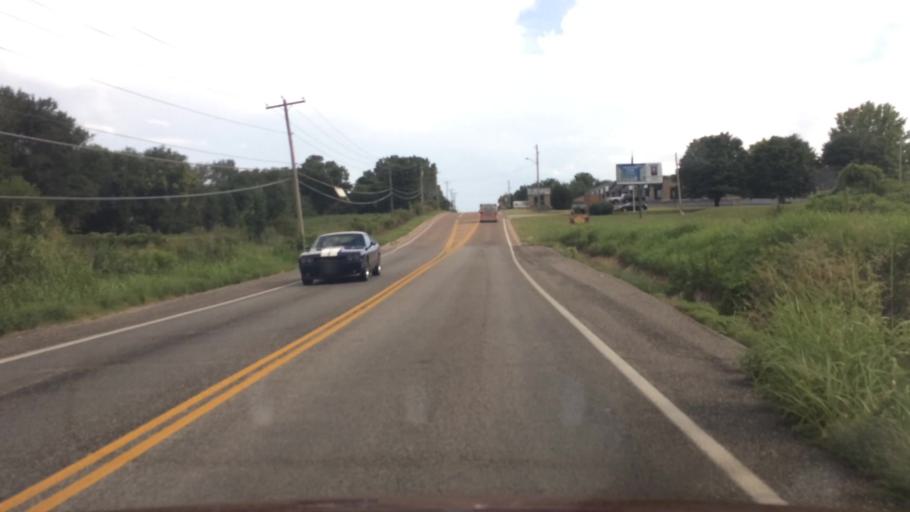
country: US
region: Missouri
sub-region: Greene County
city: Springfield
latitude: 37.2674
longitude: -93.2647
